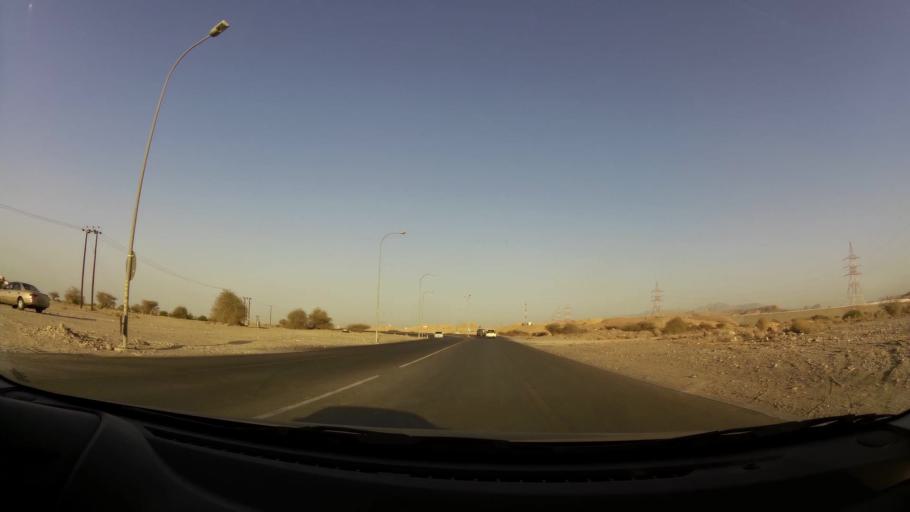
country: OM
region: Muhafazat Masqat
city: As Sib al Jadidah
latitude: 23.5735
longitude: 58.1865
